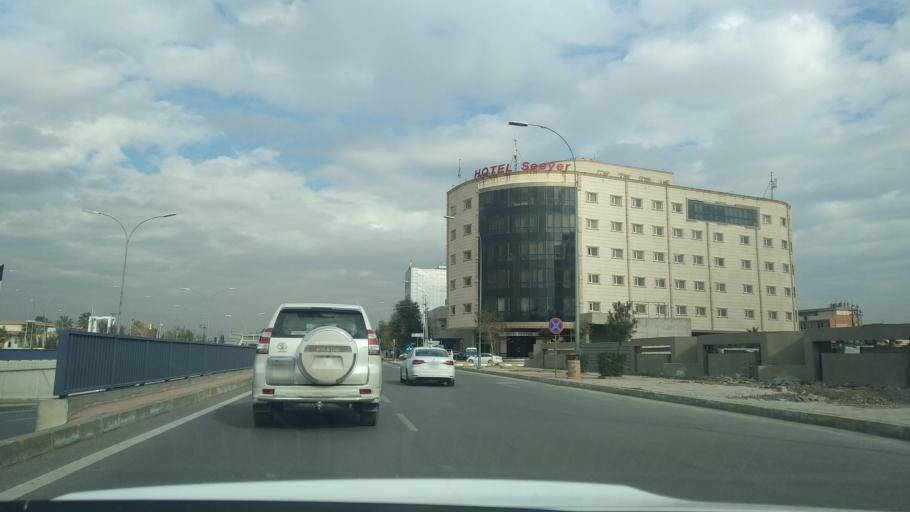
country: IQ
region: Arbil
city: Erbil
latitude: 36.1886
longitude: 43.9939
